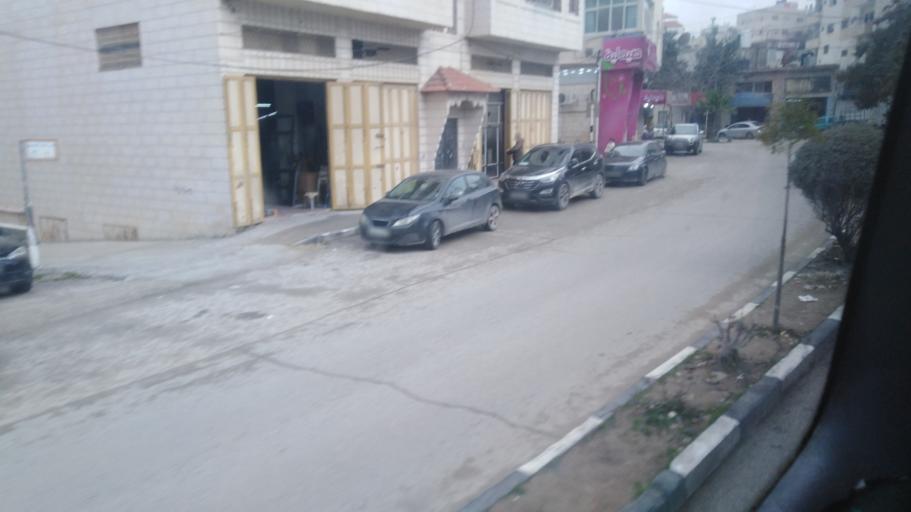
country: PS
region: West Bank
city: Hebron
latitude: 31.5289
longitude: 35.0852
